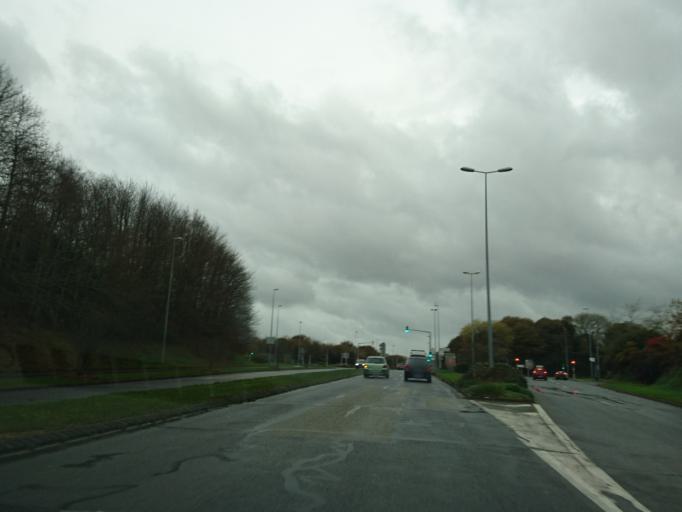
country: FR
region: Brittany
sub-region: Departement du Finistere
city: Bohars
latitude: 48.3985
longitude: -4.5292
